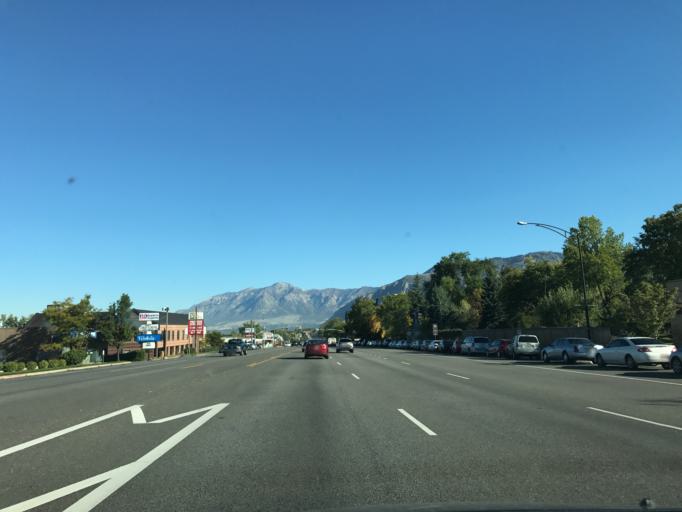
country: US
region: Utah
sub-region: Weber County
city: South Ogden
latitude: 41.1956
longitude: -111.9488
